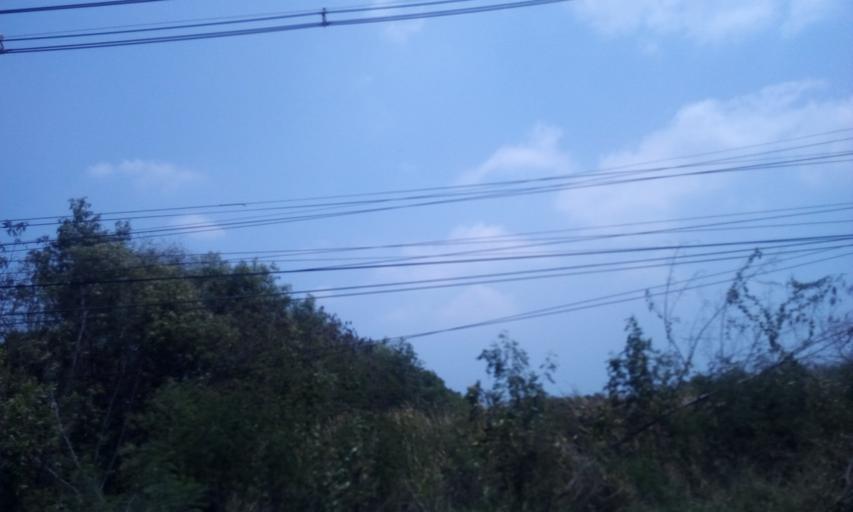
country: TH
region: Chachoengsao
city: Chachoengsao
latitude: 13.7328
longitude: 101.0872
